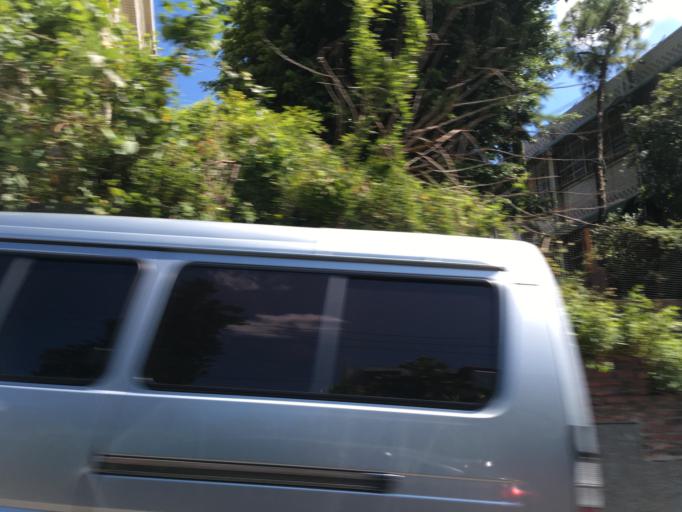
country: TW
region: Taipei
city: Taipei
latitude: 25.1433
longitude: 121.5012
